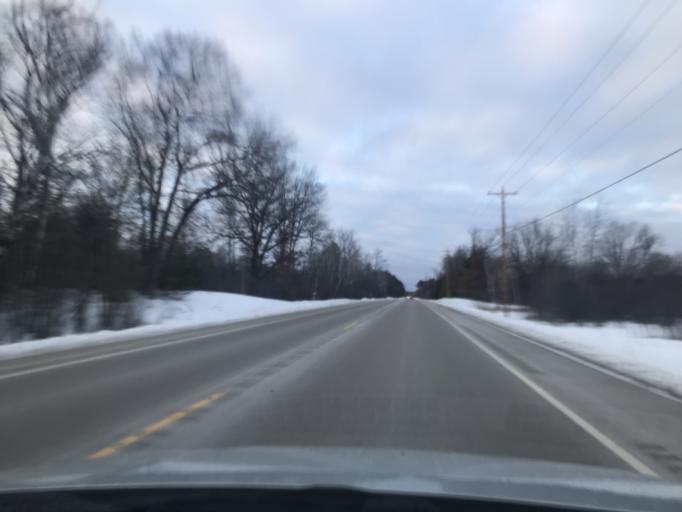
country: US
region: Wisconsin
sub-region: Marinette County
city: Marinette
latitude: 45.1241
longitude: -87.6842
